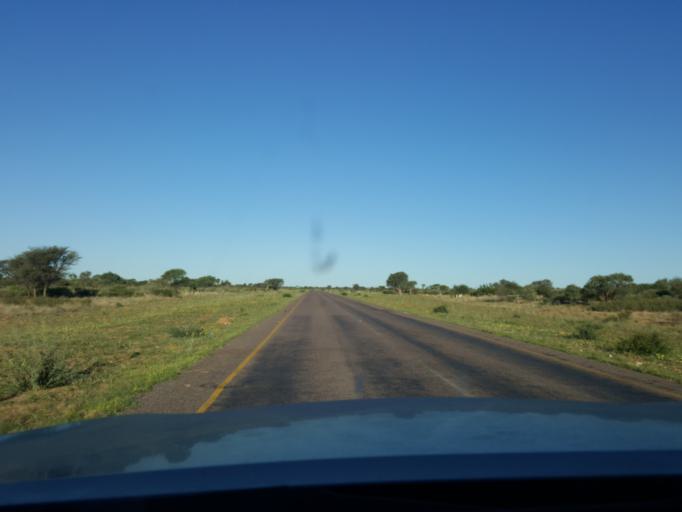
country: BW
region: Southern
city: Khakhea
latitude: -24.2996
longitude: 23.3860
